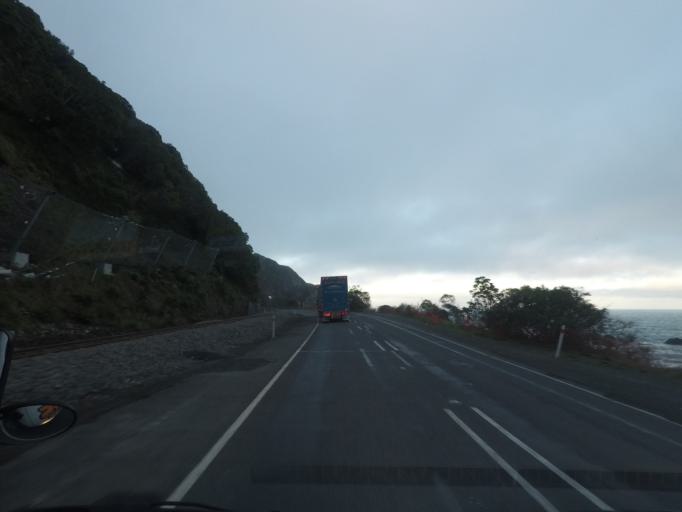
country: NZ
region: Canterbury
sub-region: Kaikoura District
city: Kaikoura
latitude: -42.4505
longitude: 173.5711
